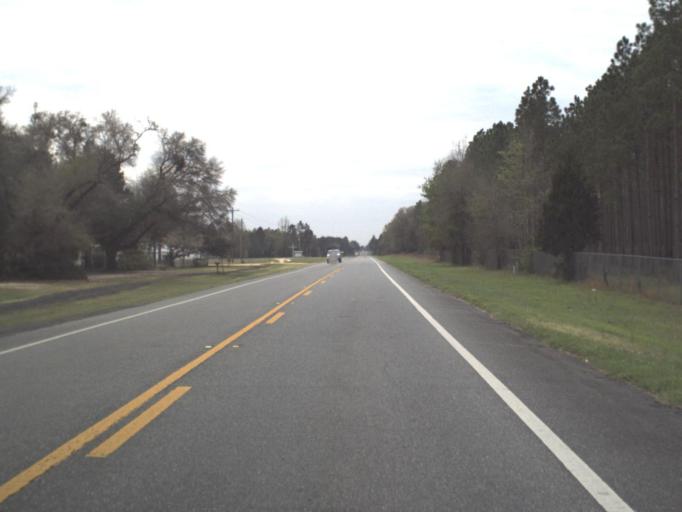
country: US
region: Florida
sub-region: Calhoun County
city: Blountstown
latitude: 30.5092
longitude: -85.2003
